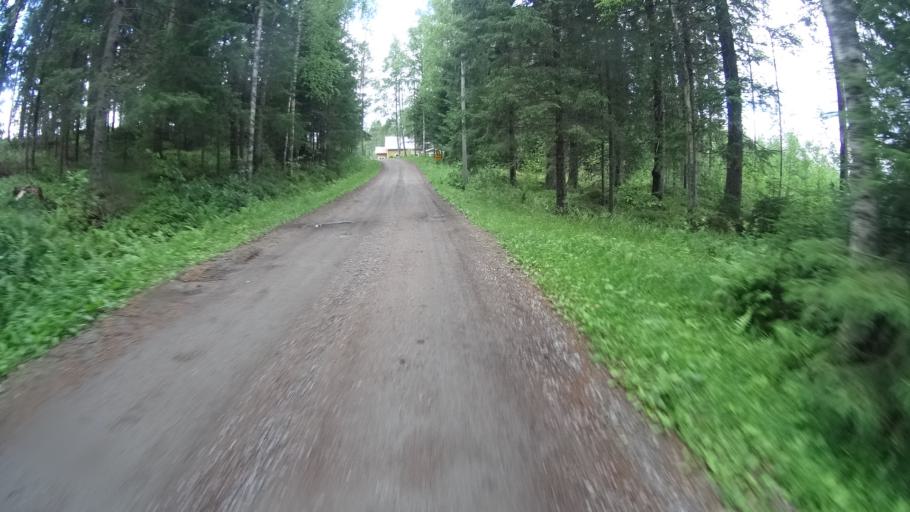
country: FI
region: Uusimaa
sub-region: Helsinki
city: Karkkila
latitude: 60.6017
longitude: 24.2083
